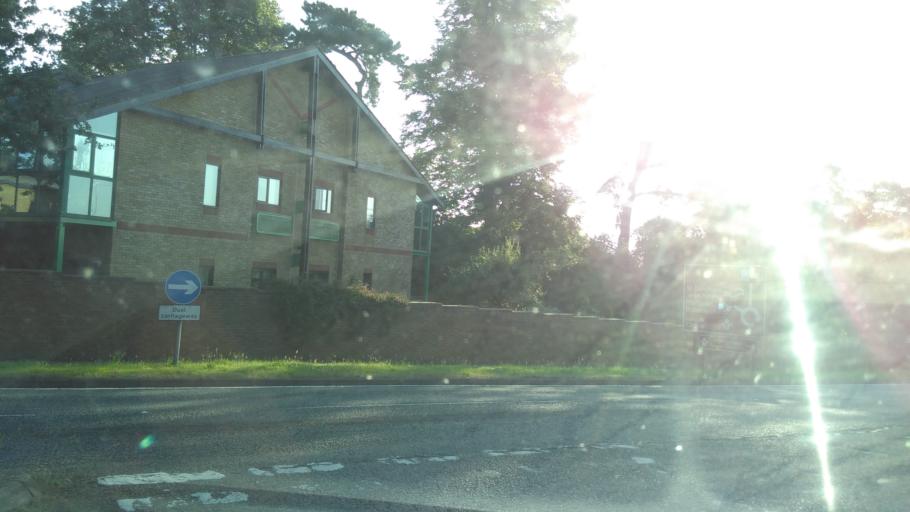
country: GB
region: England
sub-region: Kent
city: Canterbury
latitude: 51.2818
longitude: 1.0605
